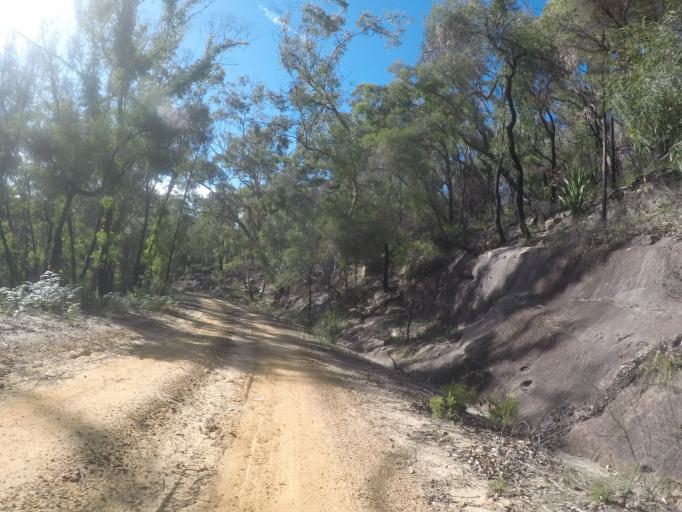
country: AU
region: New South Wales
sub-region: Hornsby Shire
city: Glenorie
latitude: -33.3340
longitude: 151.0716
